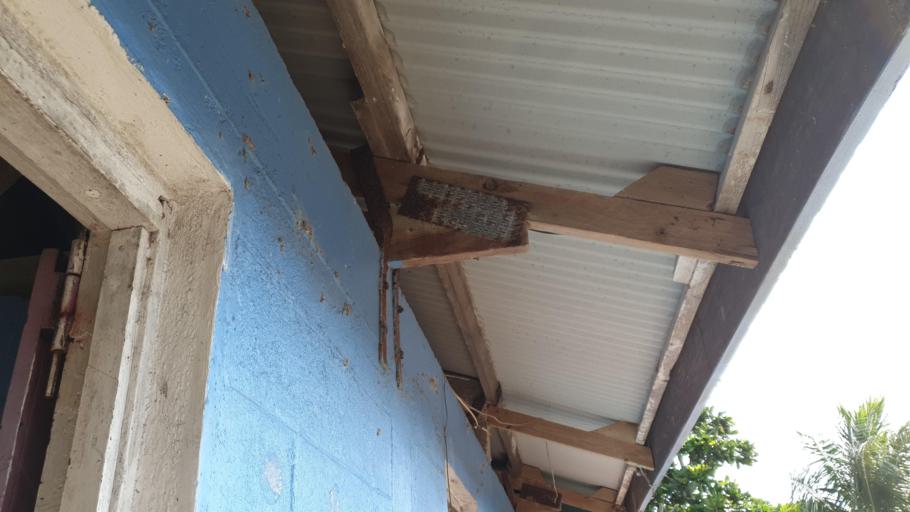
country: VU
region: Shefa
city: Port-Vila
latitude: -17.1300
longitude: 168.4305
